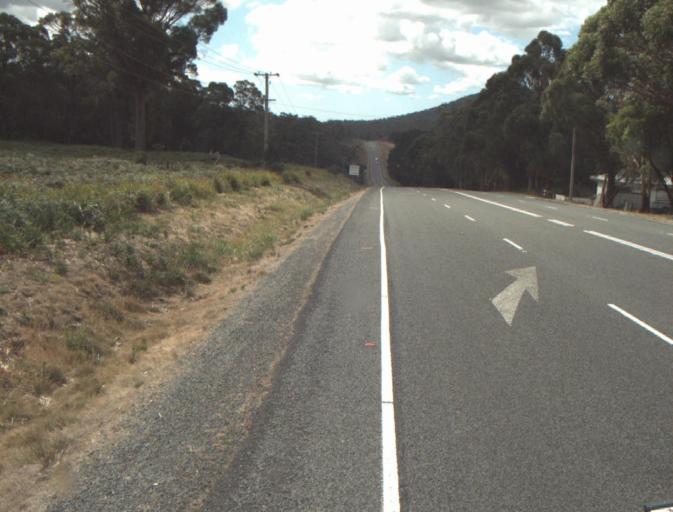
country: AU
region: Tasmania
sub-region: Launceston
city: Mayfield
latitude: -41.2779
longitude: 147.0375
